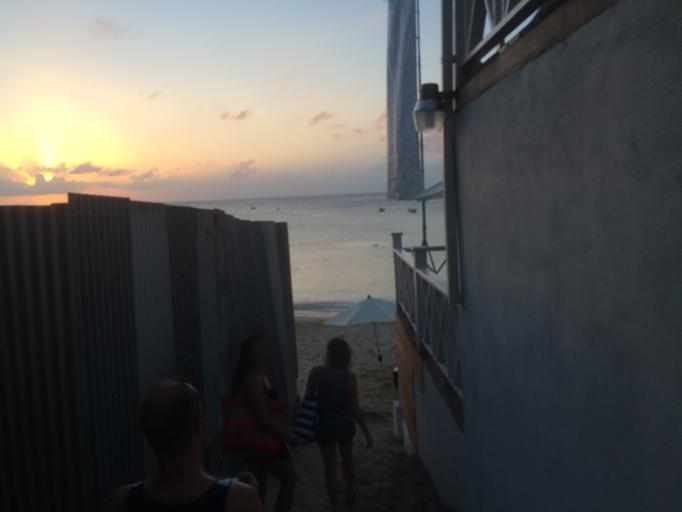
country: BB
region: Saint James
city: Holetown
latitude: 13.2057
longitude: -59.6398
